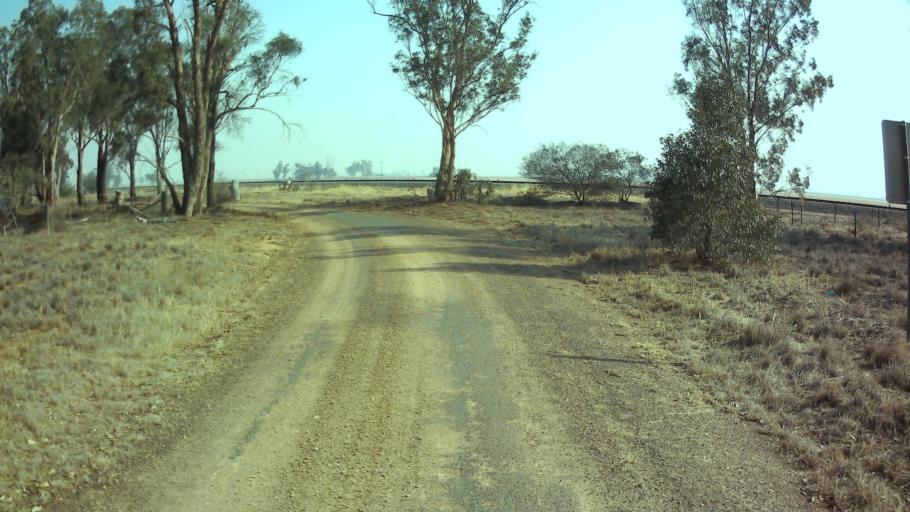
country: AU
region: New South Wales
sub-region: Weddin
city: Grenfell
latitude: -34.0081
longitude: 147.7919
